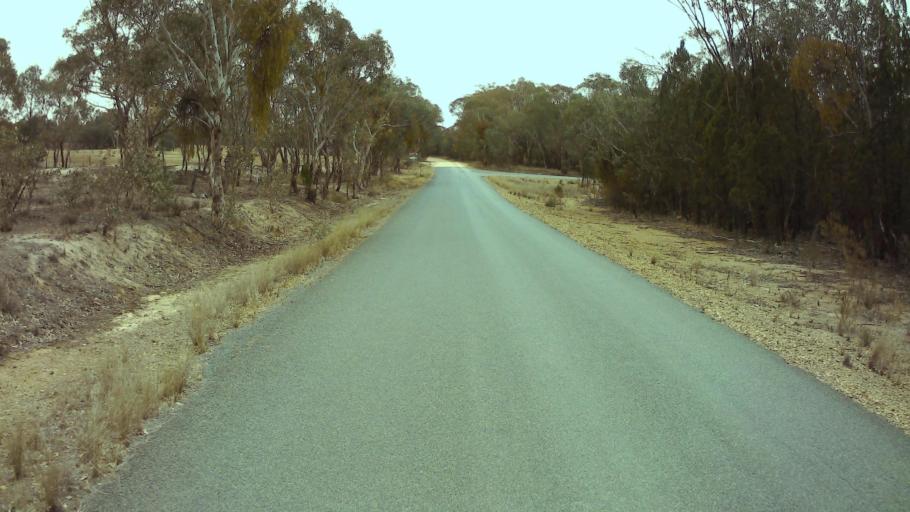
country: AU
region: New South Wales
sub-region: Weddin
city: Grenfell
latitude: -33.8841
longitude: 148.1506
